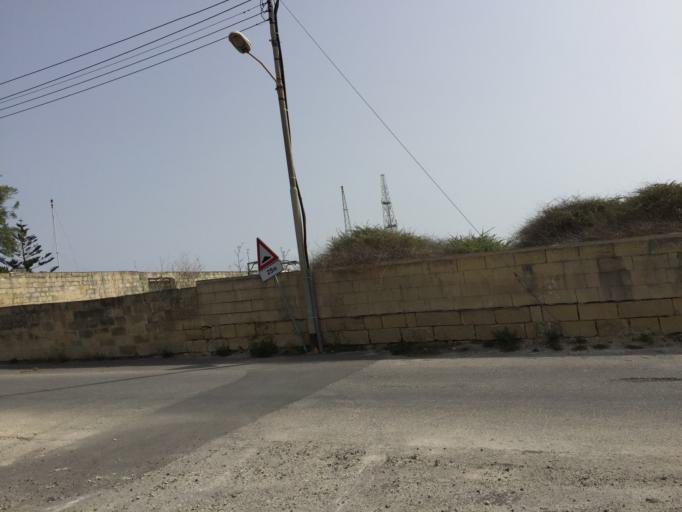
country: MT
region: Il-Kalkara
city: Kalkara
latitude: 35.8947
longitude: 14.5298
